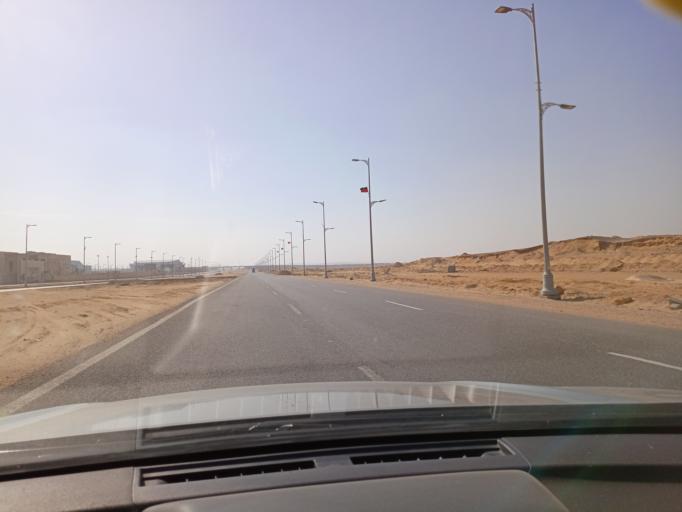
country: EG
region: Muhafazat al Qalyubiyah
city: Al Khankah
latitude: 30.0444
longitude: 31.7025
